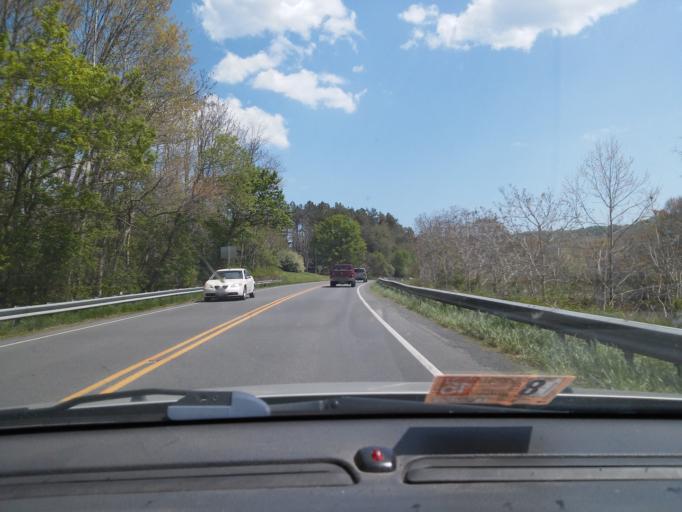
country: US
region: Virginia
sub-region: Warren County
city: Front Royal
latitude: 38.8888
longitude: -78.1703
